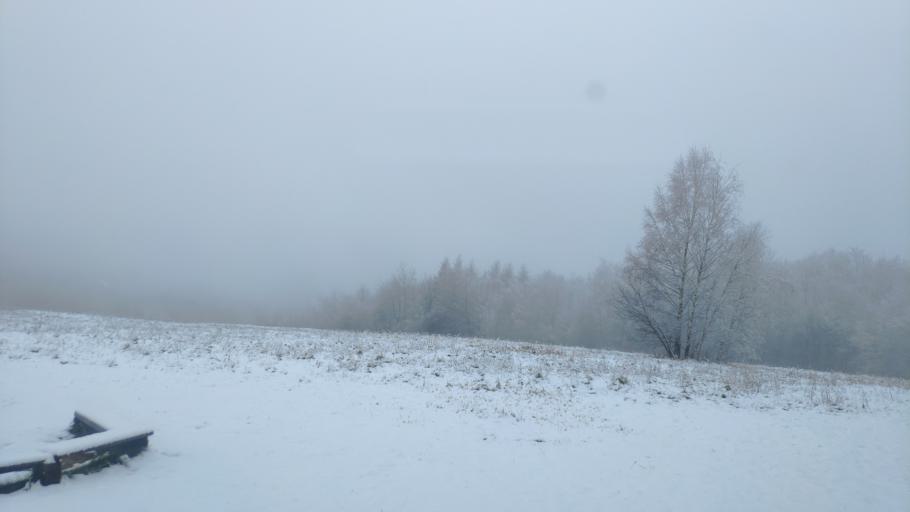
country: SK
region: Kosicky
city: Moldava nad Bodvou
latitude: 48.7382
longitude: 21.0968
